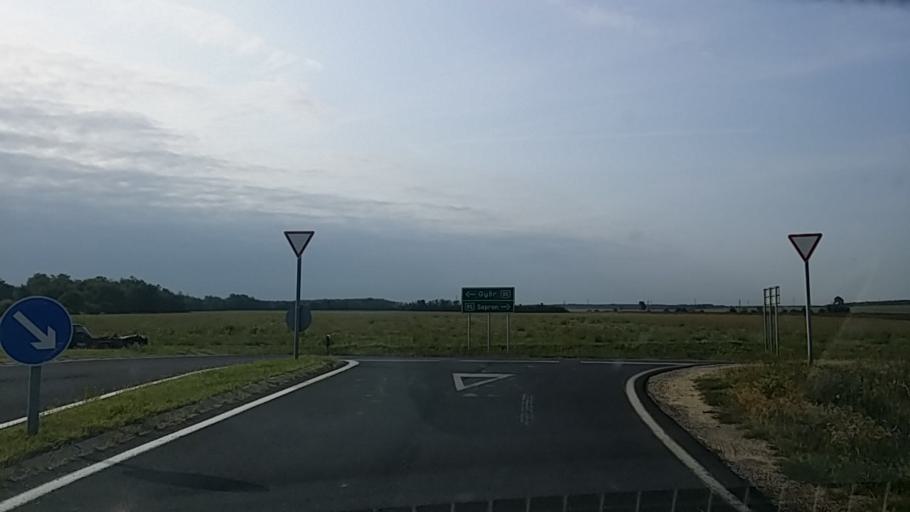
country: HU
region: Gyor-Moson-Sopron
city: Fertoszentmiklos
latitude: 47.5975
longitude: 16.9164
